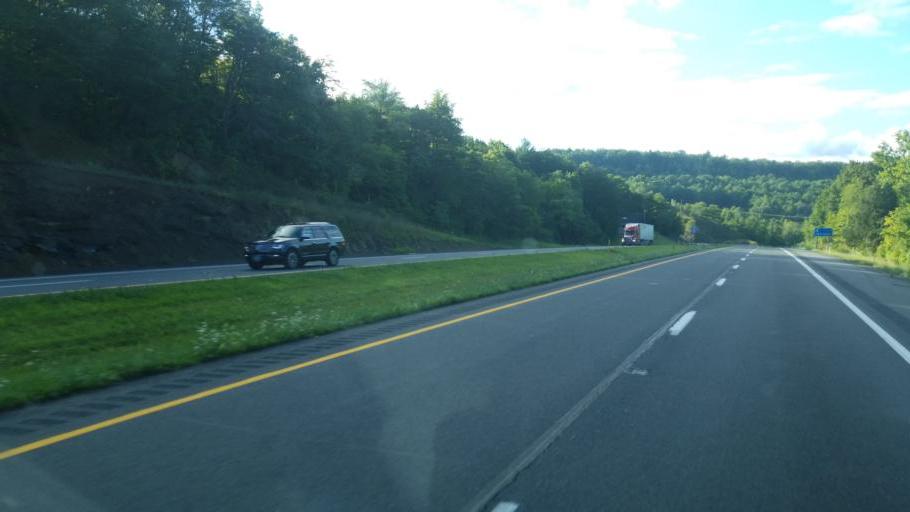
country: US
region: Maryland
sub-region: Washington County
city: Hancock
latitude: 39.7780
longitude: -78.2021
